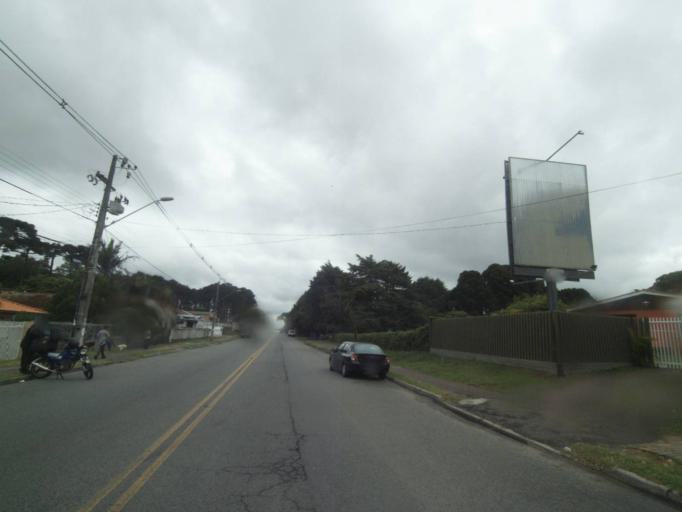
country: BR
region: Parana
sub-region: Curitiba
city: Curitiba
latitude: -25.4477
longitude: -49.3497
